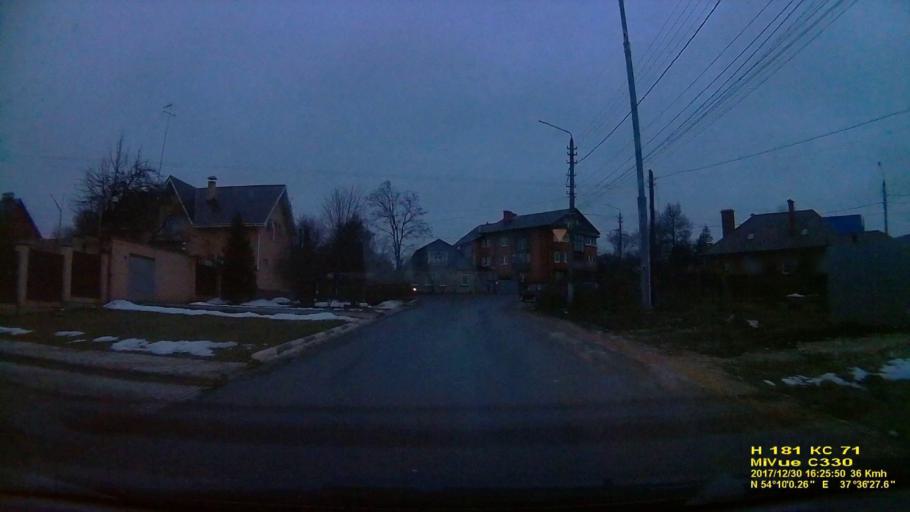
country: RU
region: Tula
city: Tula
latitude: 54.1666
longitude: 37.6078
